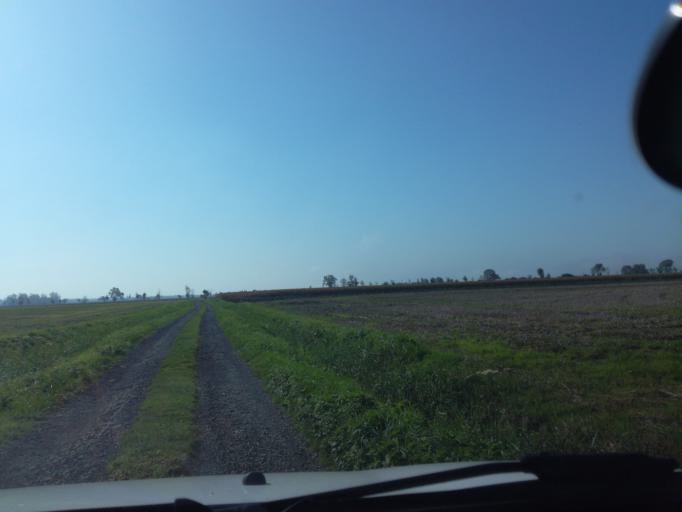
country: FR
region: Brittany
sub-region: Departement d'Ille-et-Vilaine
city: Cherrueix
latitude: 48.5924
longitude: -1.6840
